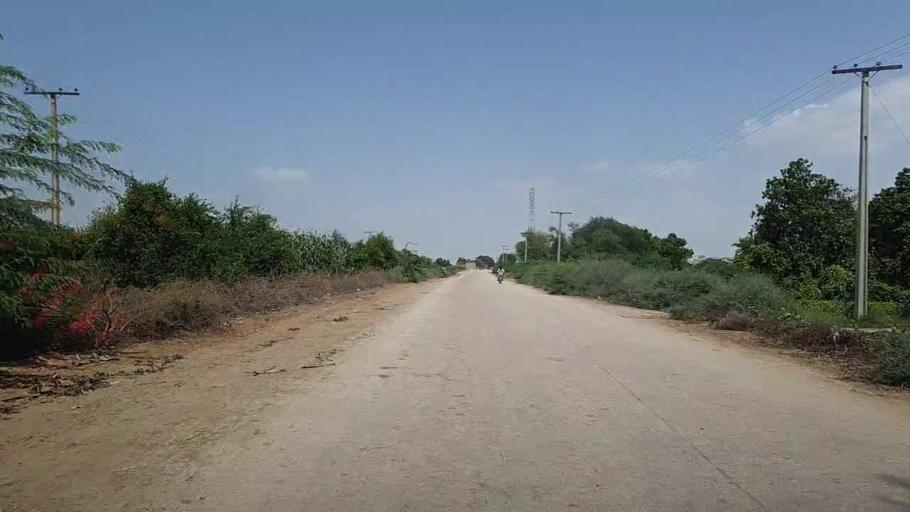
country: PK
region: Sindh
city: Pad Idan
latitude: 26.7840
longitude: 68.3341
